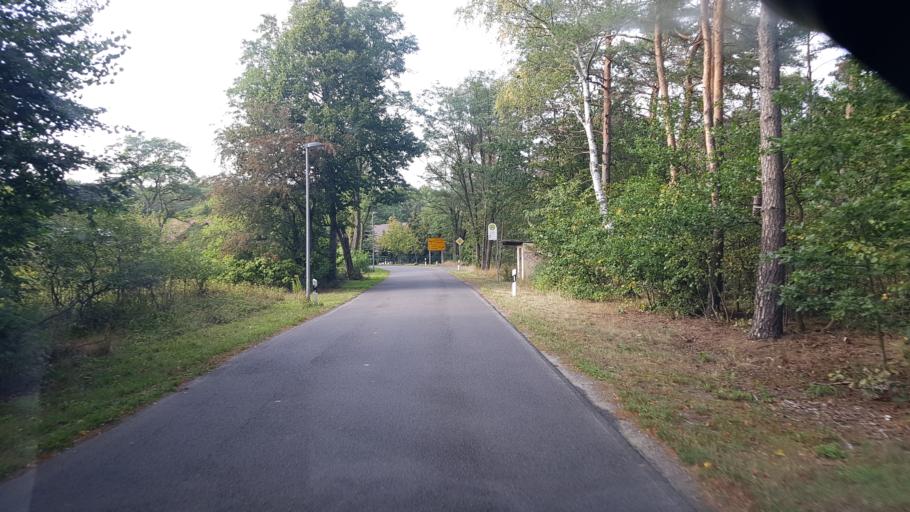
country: DE
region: Brandenburg
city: Neupetershain
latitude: 51.5885
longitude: 14.1138
